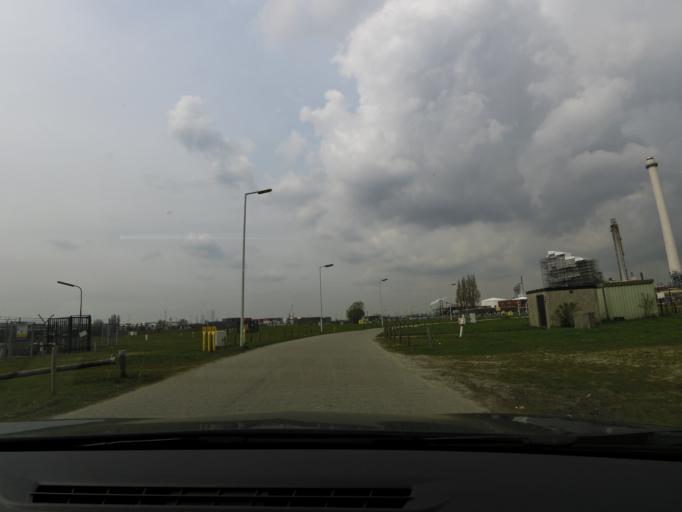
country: NL
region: South Holland
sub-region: Gemeente Spijkenisse
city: Spijkenisse
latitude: 51.8745
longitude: 4.3330
